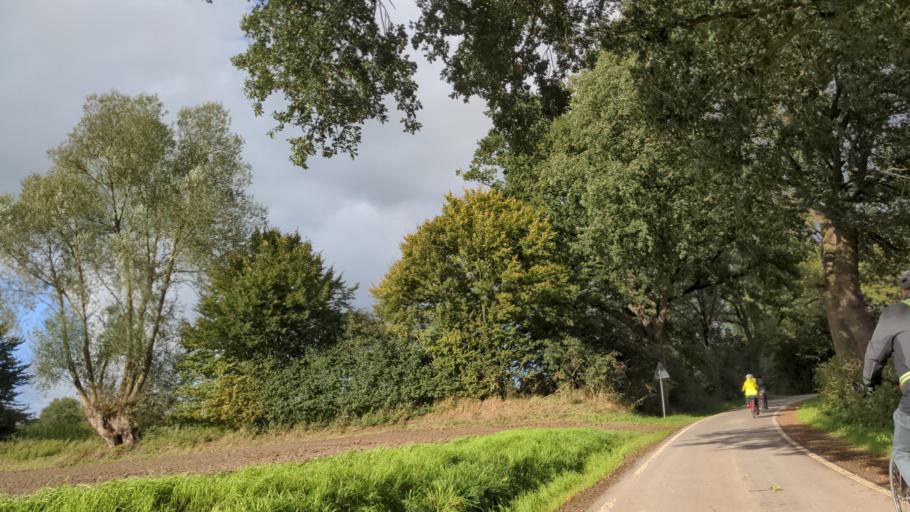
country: DE
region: Schleswig-Holstein
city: Hamberge
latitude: 53.8098
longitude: 10.6118
